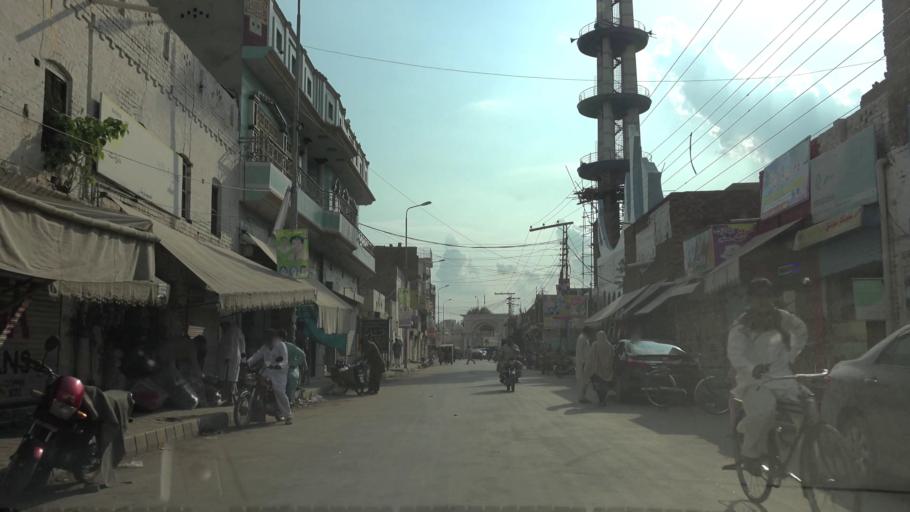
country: PK
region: Punjab
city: Nankana Sahib
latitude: 31.4472
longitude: 73.6990
